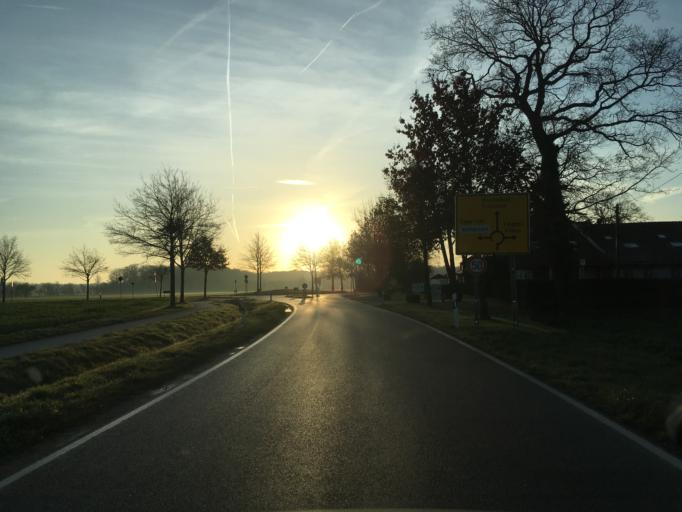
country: DE
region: North Rhine-Westphalia
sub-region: Regierungsbezirk Munster
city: Schoppingen
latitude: 52.0539
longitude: 7.2298
